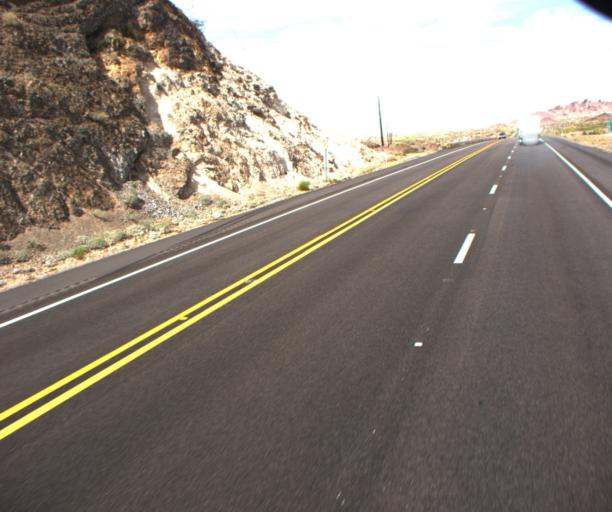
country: US
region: Arizona
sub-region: Mohave County
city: Desert Hills
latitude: 34.6133
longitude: -114.3507
